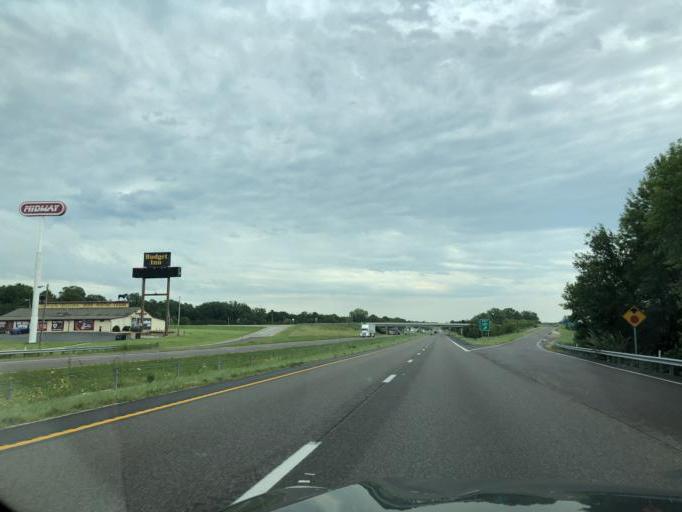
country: US
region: Missouri
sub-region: Boone County
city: Columbia
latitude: 38.9717
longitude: -92.4346
